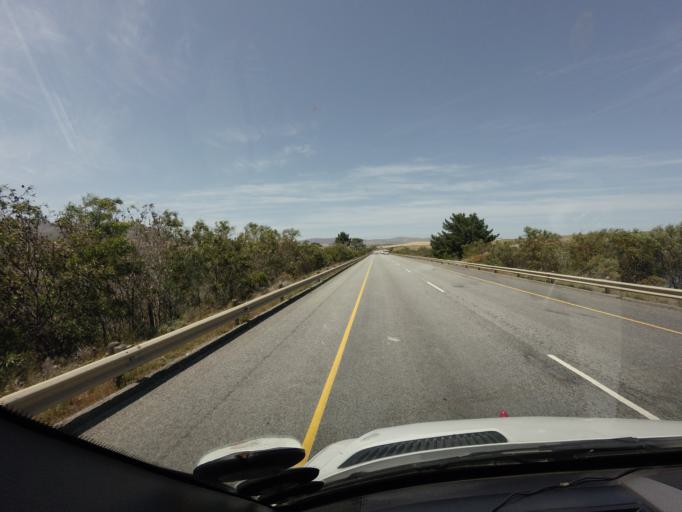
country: ZA
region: Western Cape
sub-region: Overberg District Municipality
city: Hermanus
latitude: -34.3097
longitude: 19.1468
